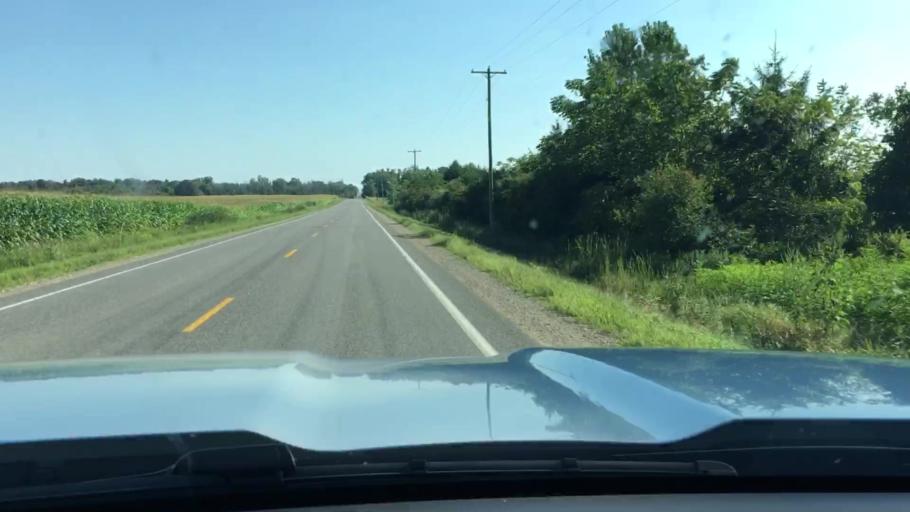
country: US
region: Michigan
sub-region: Muskegon County
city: Ravenna
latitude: 43.1536
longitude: -85.9278
